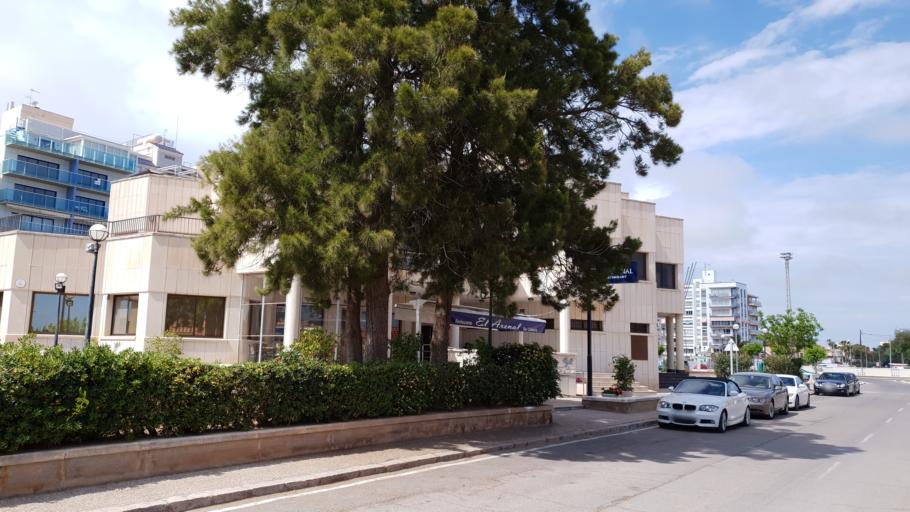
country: ES
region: Valencia
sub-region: Provincia de Castello
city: Burriana
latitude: 39.8648
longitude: -0.0724
